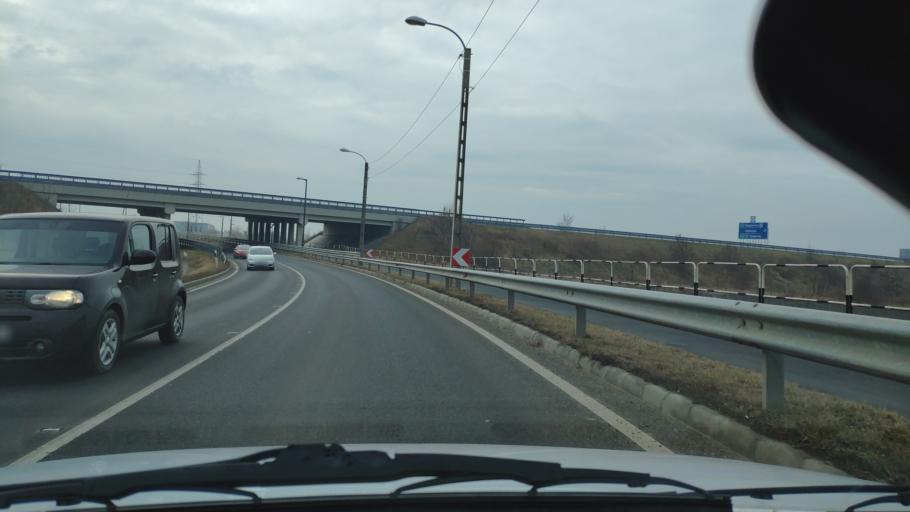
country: HU
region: Zala
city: Nagykanizsa
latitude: 46.4790
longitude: 16.9850
